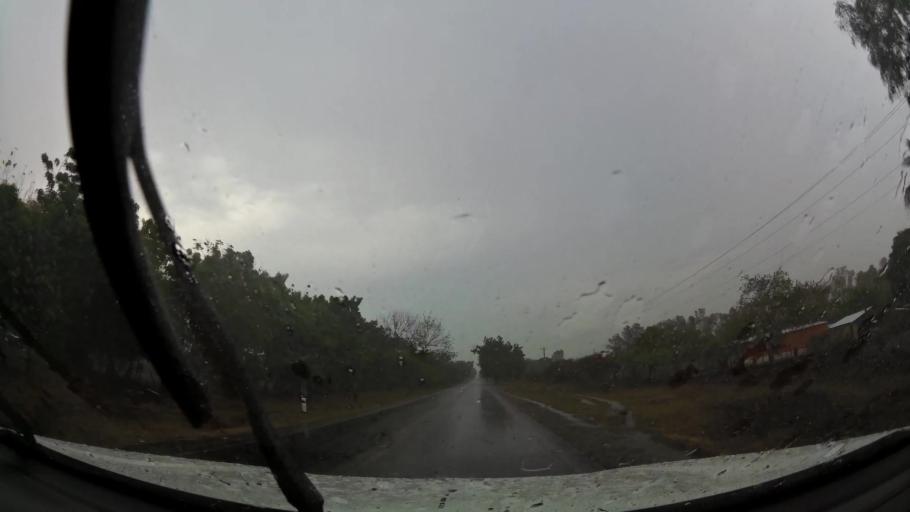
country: NI
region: Leon
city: Telica
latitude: 12.5295
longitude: -86.8555
